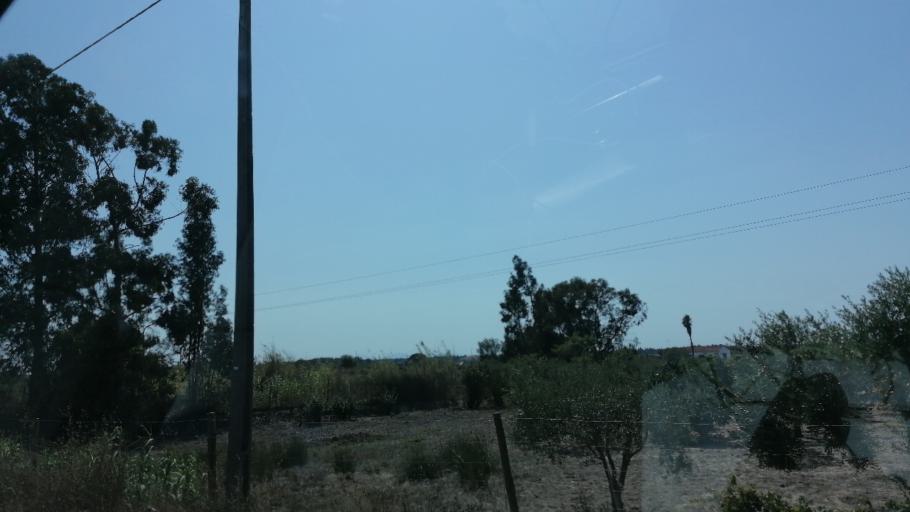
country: PT
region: Evora
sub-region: Vendas Novas
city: Vendas Novas
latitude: 38.6954
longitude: -8.6118
